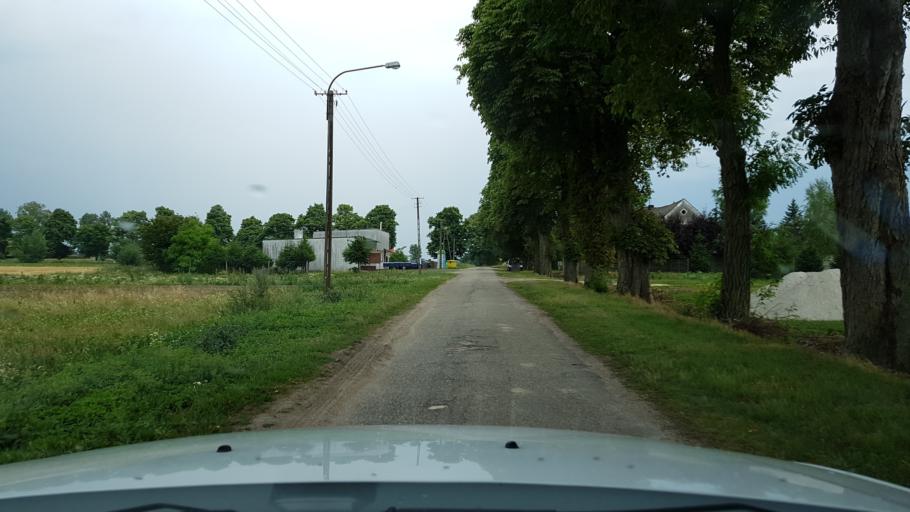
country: PL
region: West Pomeranian Voivodeship
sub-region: Powiat walecki
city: Walcz
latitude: 53.3526
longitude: 16.3589
